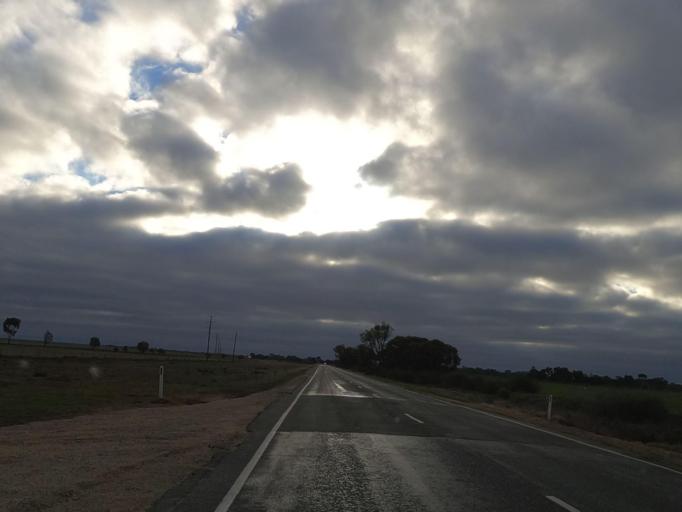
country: AU
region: Victoria
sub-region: Swan Hill
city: Swan Hill
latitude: -35.6552
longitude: 143.8499
